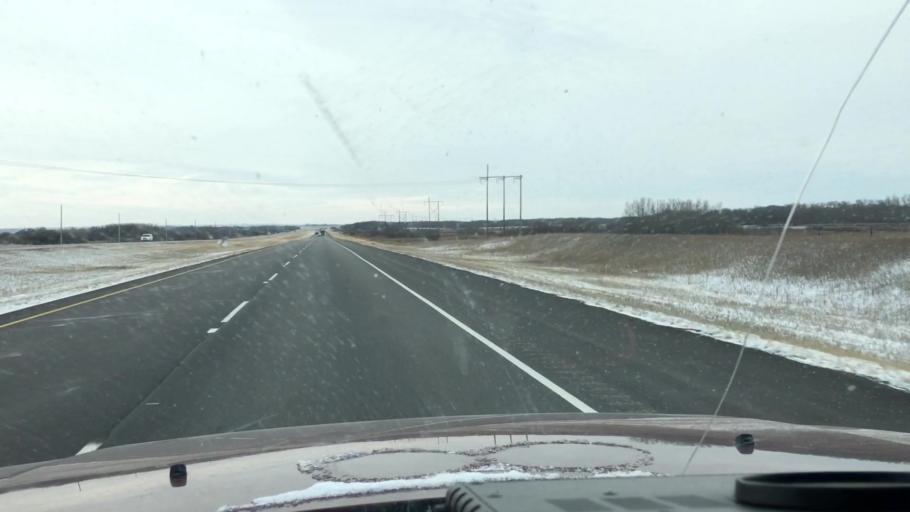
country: CA
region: Saskatchewan
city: Saskatoon
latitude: 51.8928
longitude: -106.5180
